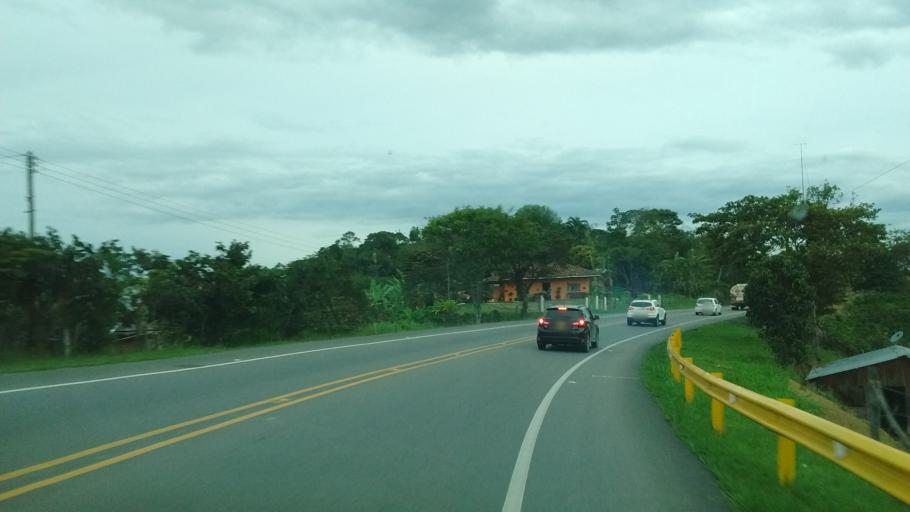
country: CO
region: Cauca
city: Morales
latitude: 2.7715
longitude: -76.5554
